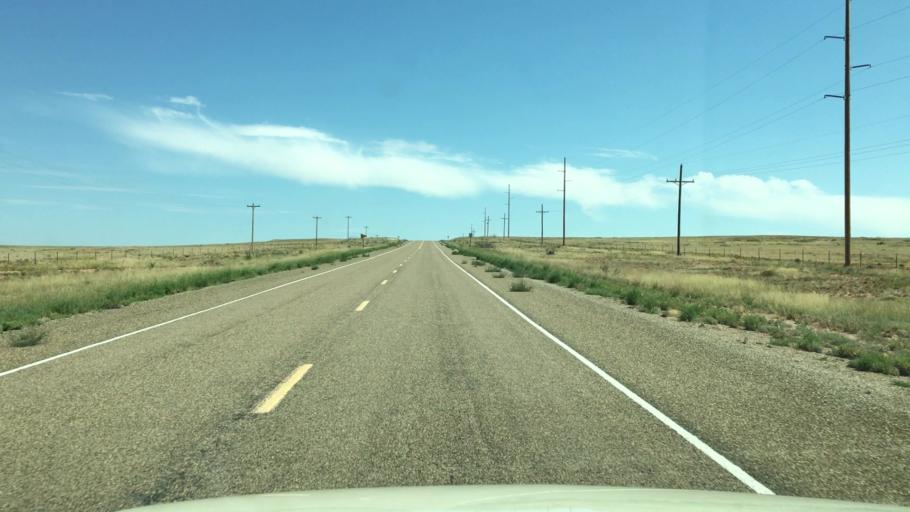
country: US
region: New Mexico
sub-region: Chaves County
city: Roswell
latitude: 33.9338
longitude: -104.5957
